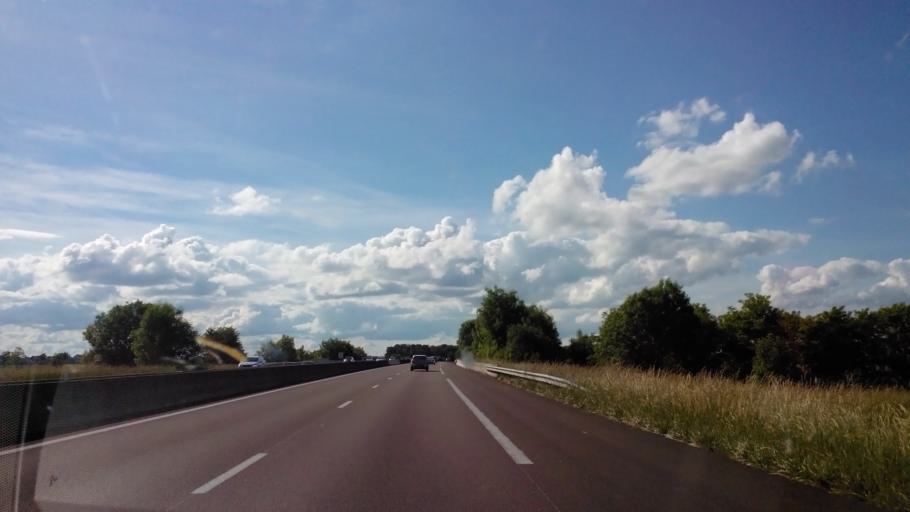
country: FR
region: Bourgogne
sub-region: Departement de la Cote-d'Or
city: Pouilly-en-Auxois
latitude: 47.2149
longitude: 4.6047
